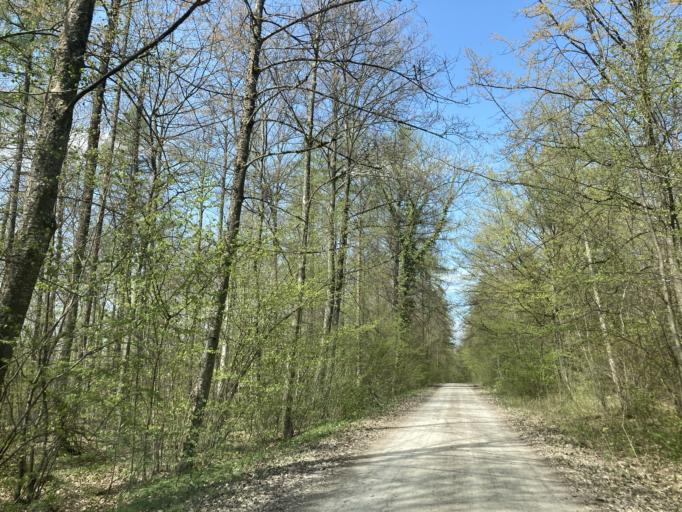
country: DE
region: Baden-Wuerttemberg
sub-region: Tuebingen Region
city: Bodelshausen
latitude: 48.4349
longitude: 8.9862
